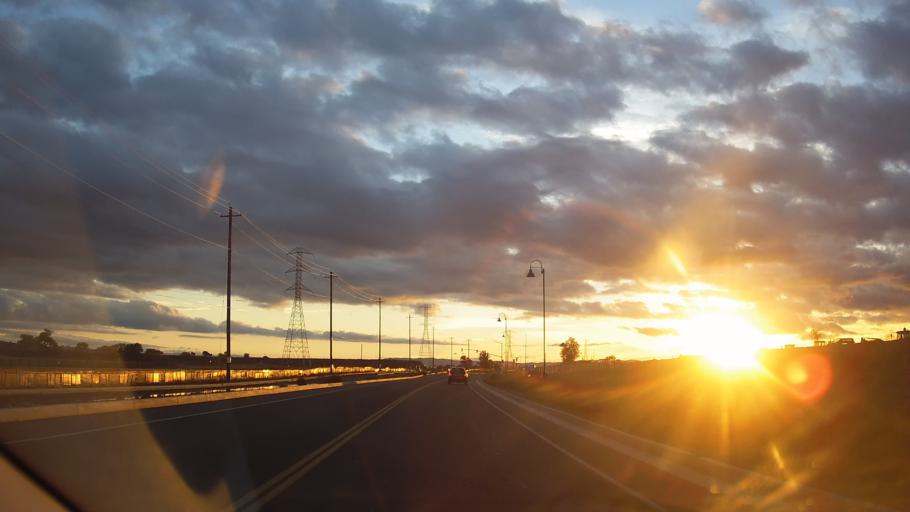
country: US
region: California
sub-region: Solano County
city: Vacaville
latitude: 38.2931
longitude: -121.9557
